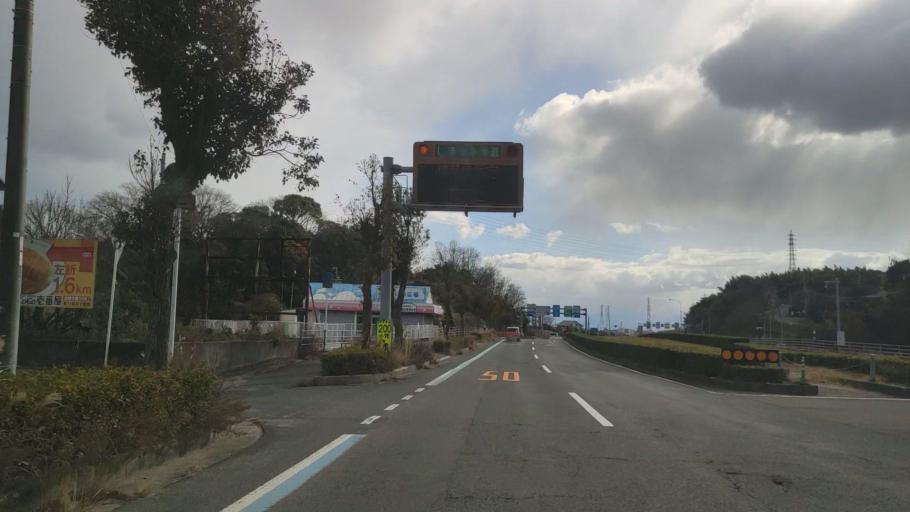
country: JP
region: Ehime
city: Hojo
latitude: 34.0566
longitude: 132.9746
